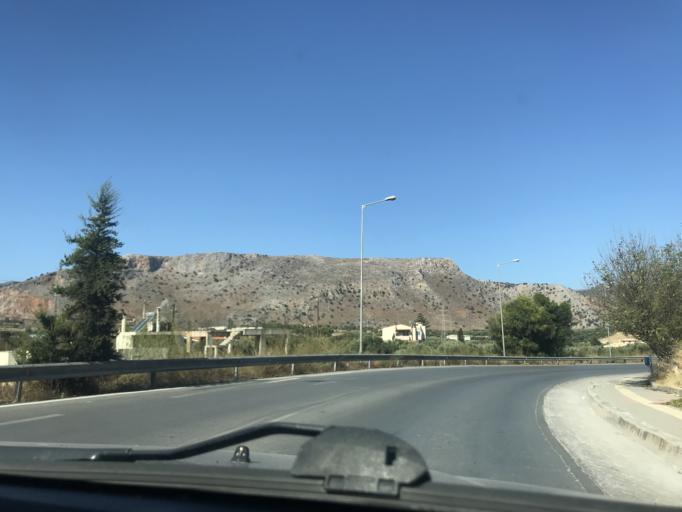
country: GR
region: Crete
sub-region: Nomos Irakleiou
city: Gazi
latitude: 35.3233
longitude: 25.0628
